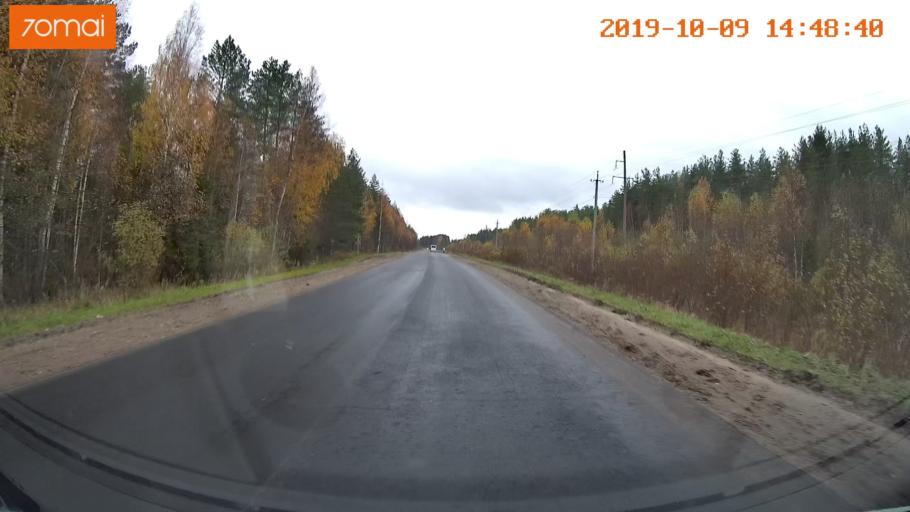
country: RU
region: Kostroma
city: Chistyye Bory
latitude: 58.4025
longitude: 41.5764
